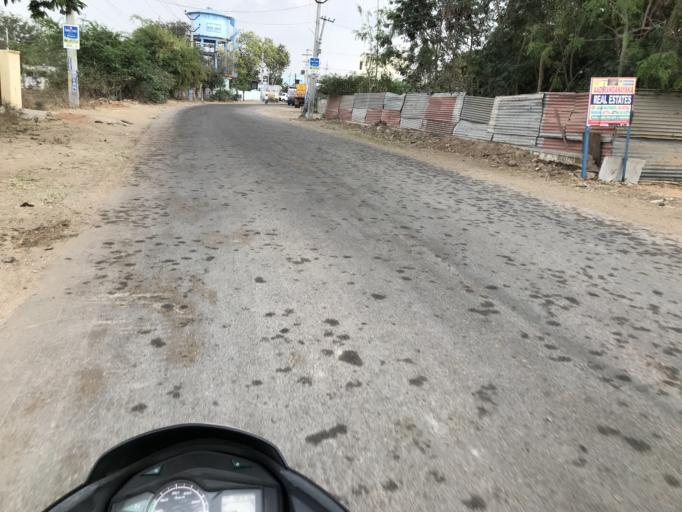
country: IN
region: Telangana
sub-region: Rangareddi
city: Lal Bahadur Nagar
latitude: 17.2851
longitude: 78.6350
